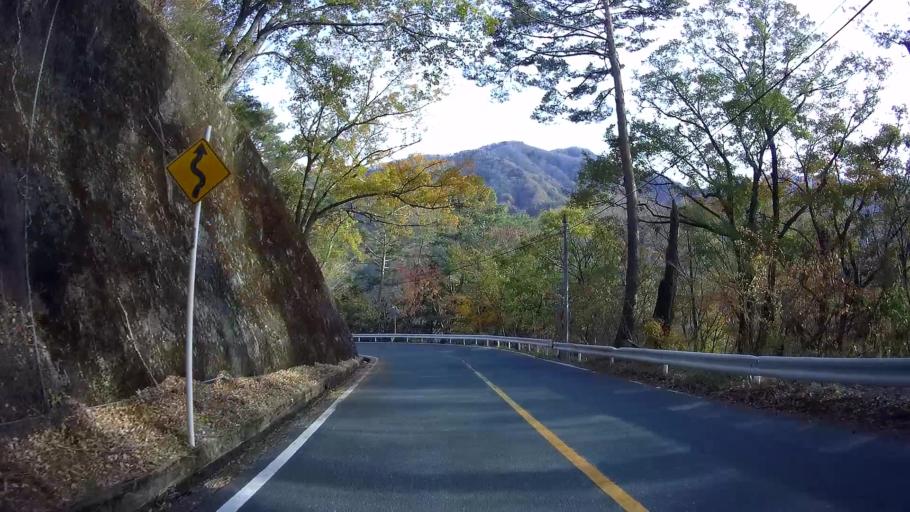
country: JP
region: Yamanashi
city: Fujikawaguchiko
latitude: 35.4781
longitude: 138.5528
